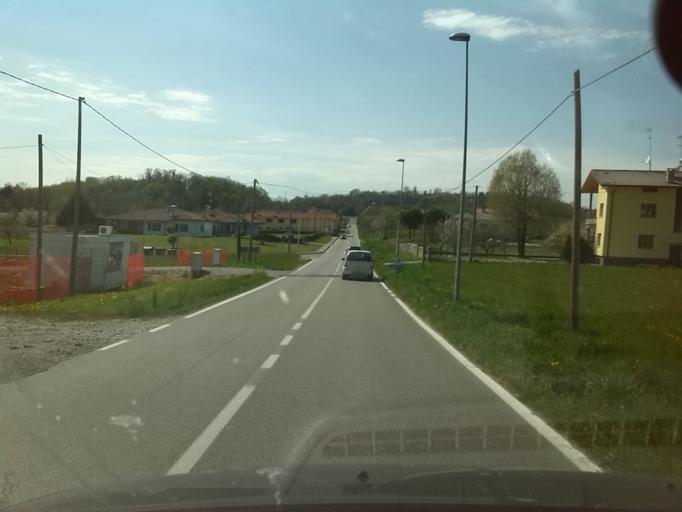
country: IT
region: Friuli Venezia Giulia
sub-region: Provincia di Udine
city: Moruzzo
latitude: 46.1166
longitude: 13.1134
